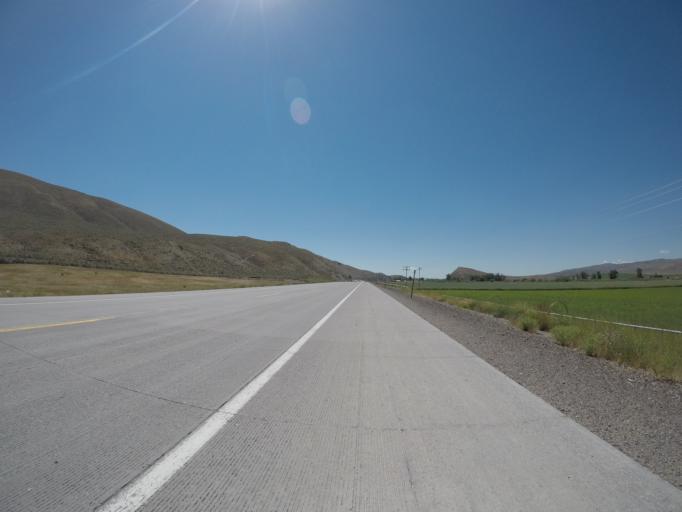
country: US
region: Idaho
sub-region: Bear Lake County
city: Montpelier
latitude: 42.1477
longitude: -110.9777
